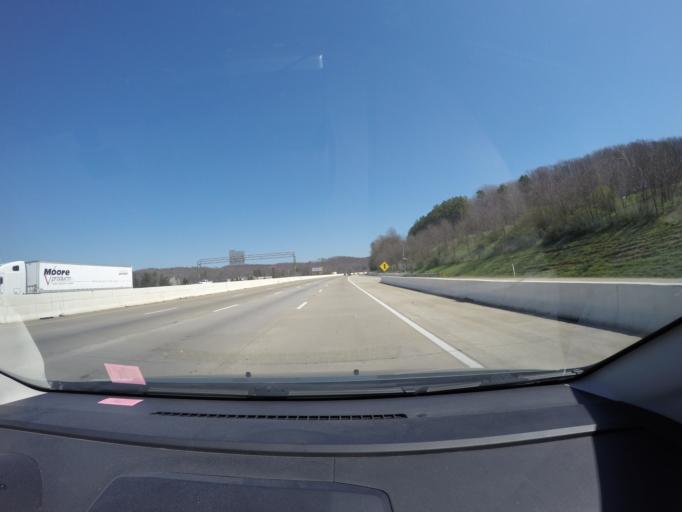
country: US
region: Tennessee
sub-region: Hamilton County
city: Harrison
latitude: 35.0635
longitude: -85.1272
